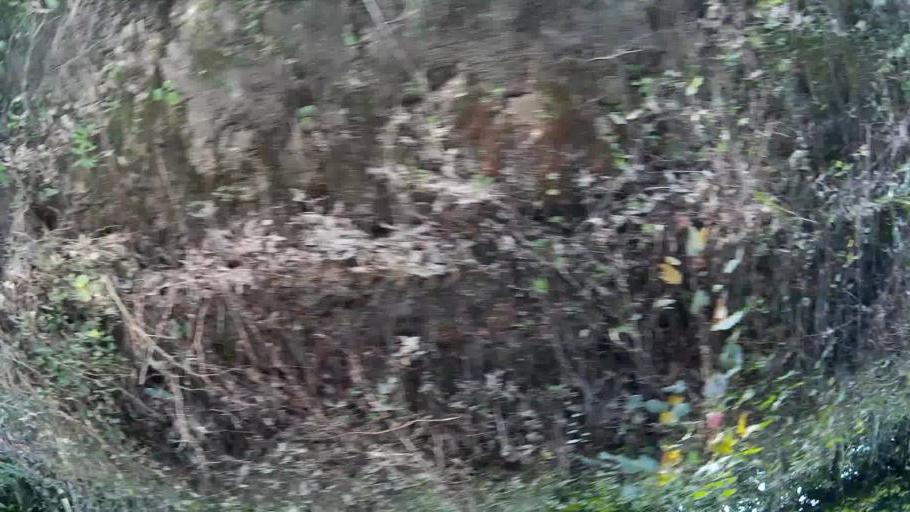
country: CO
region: Valle del Cauca
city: Ulloa
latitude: 4.7343
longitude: -75.7346
